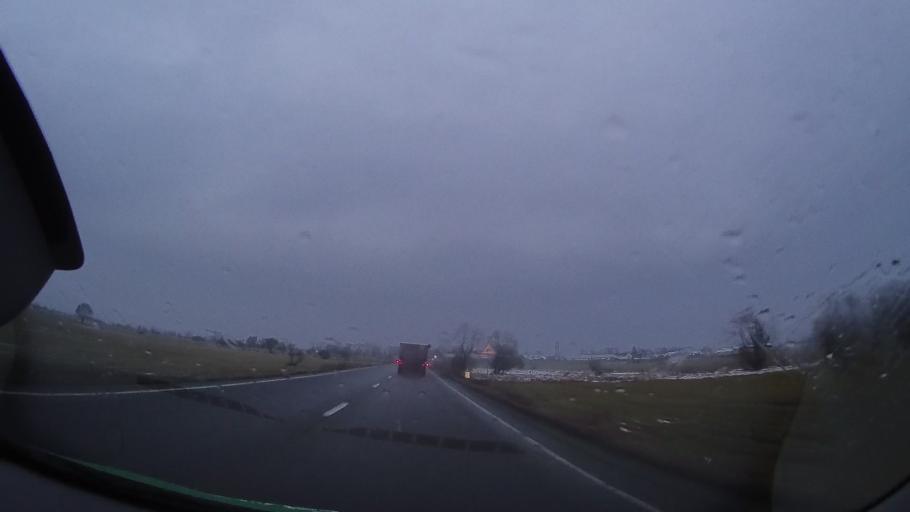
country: RO
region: Harghita
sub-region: Comuna Lazarea
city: Lazarea
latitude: 46.7614
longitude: 25.5155
